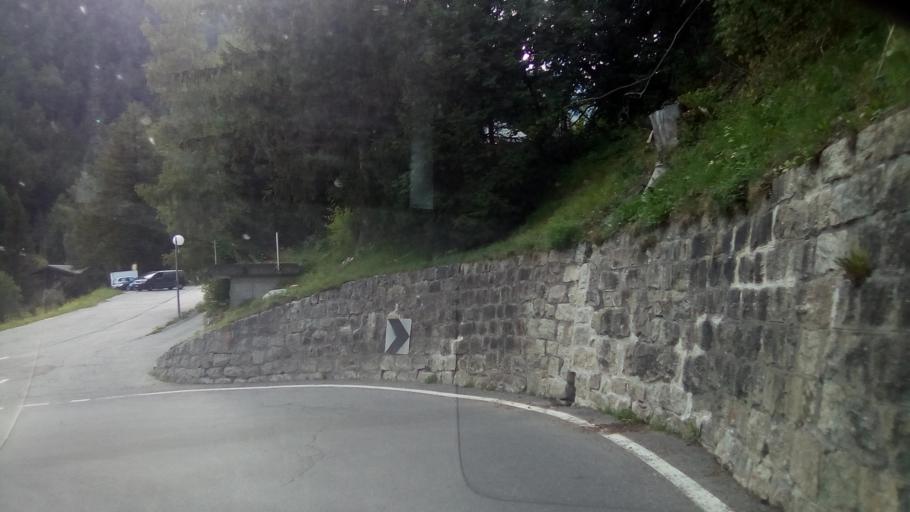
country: CH
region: Valais
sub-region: Entremont District
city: Orsieres
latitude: 46.0261
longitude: 7.1196
